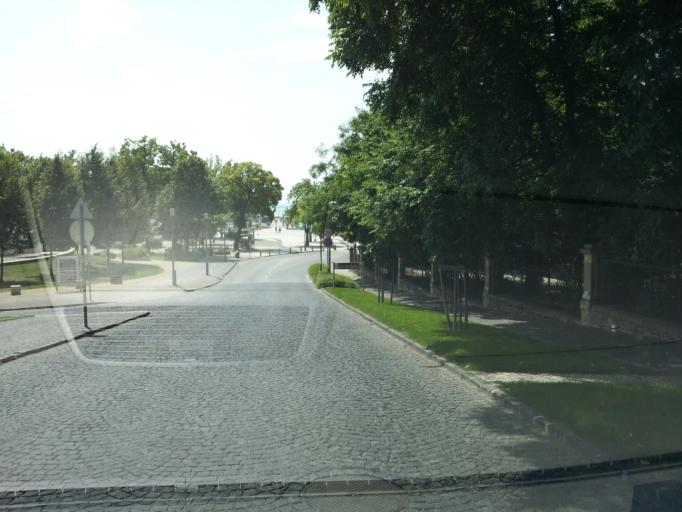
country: HU
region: Veszprem
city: Balatonfured
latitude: 46.9546
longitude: 17.8926
